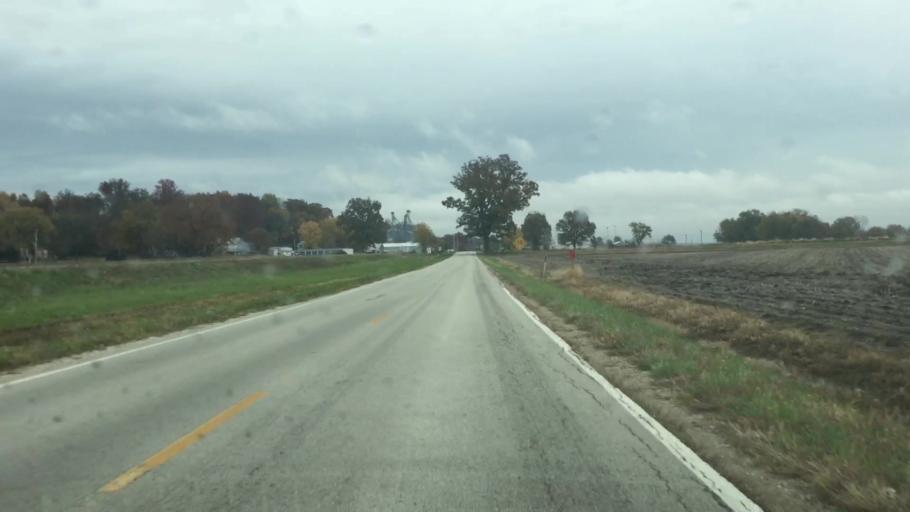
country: US
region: Missouri
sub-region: Gasconade County
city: Hermann
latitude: 38.7162
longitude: -91.5246
